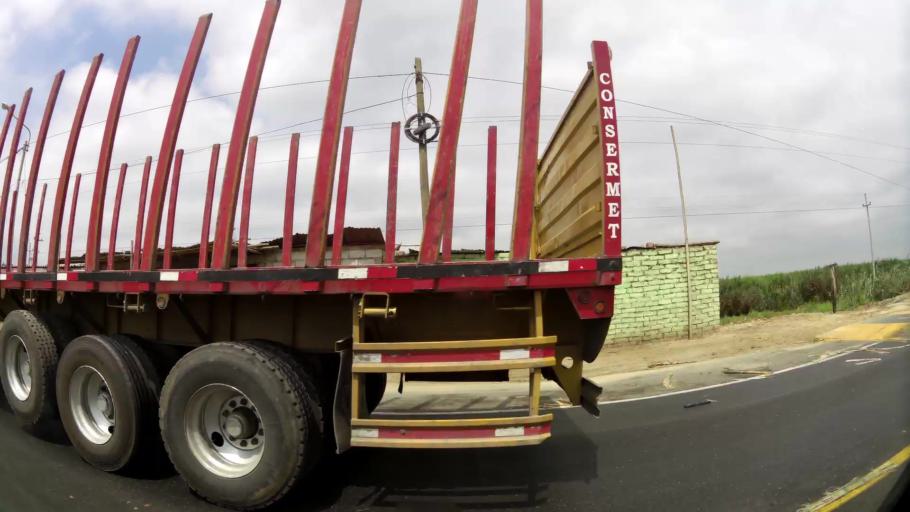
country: PE
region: La Libertad
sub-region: Ascope
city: Chocope
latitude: -7.7903
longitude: -79.2298
